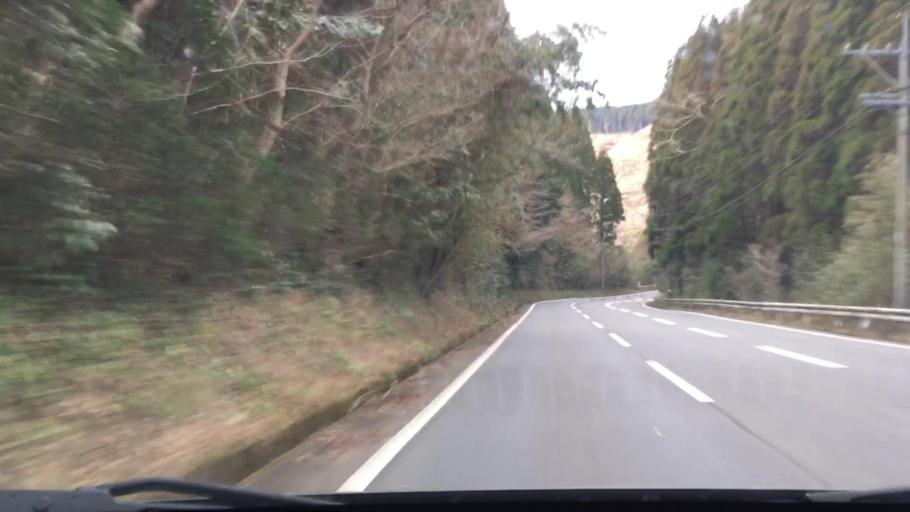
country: JP
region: Miyazaki
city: Nichinan
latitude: 31.7066
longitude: 131.3286
